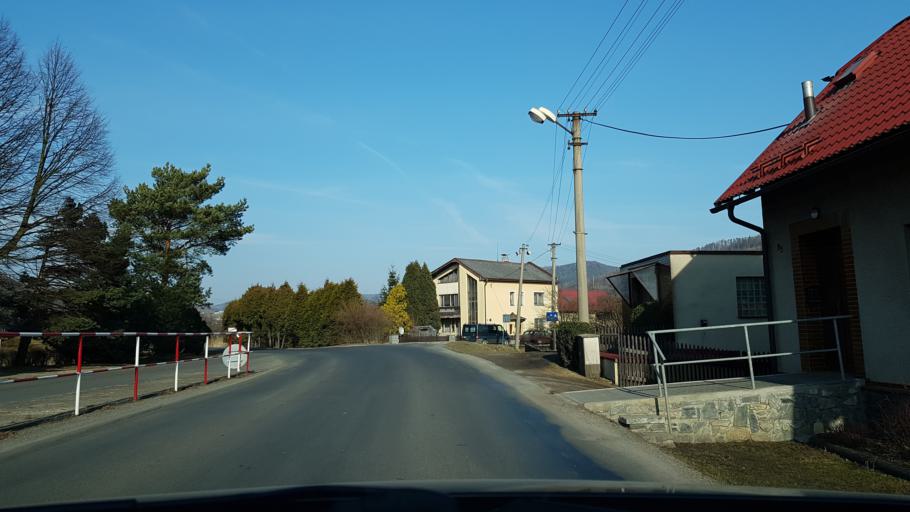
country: CZ
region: Olomoucky
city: Olsany
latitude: 49.9696
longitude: 16.8632
